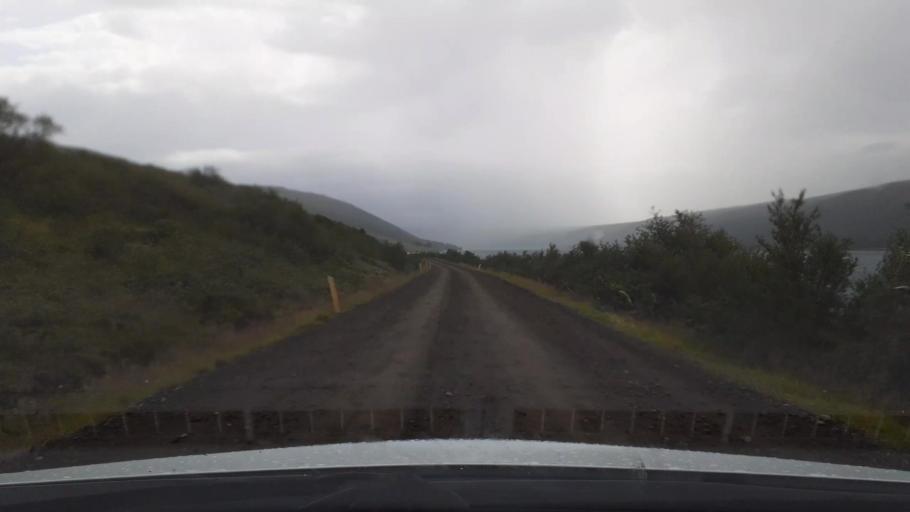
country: IS
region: Capital Region
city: Mosfellsbaer
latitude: 64.5128
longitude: -21.4042
